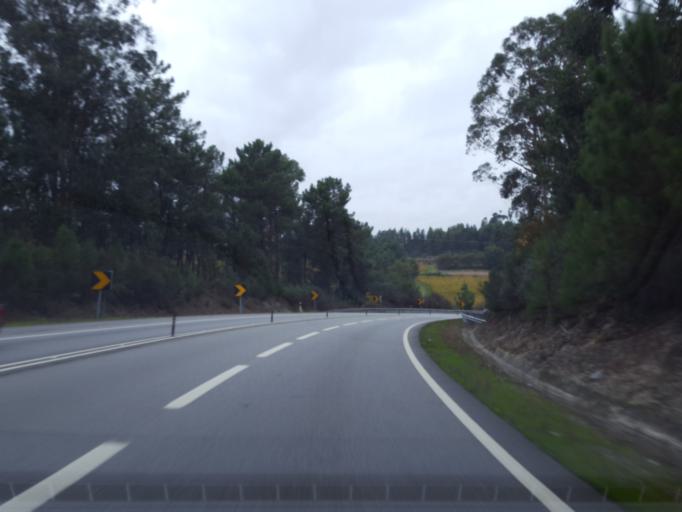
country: PT
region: Porto
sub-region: Lousada
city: Meinedo
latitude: 41.2288
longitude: -8.1999
